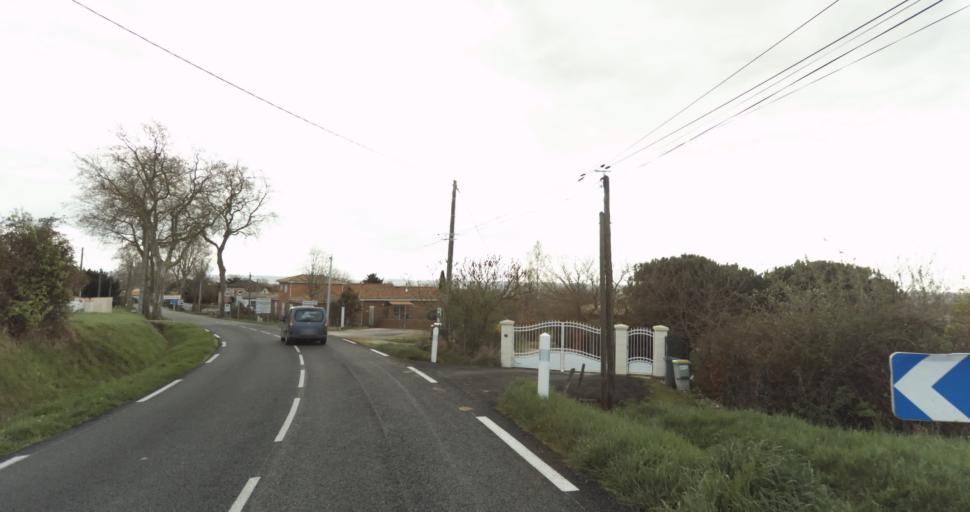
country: FR
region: Midi-Pyrenees
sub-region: Departement de la Haute-Garonne
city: Auterive
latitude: 43.3574
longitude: 1.4853
